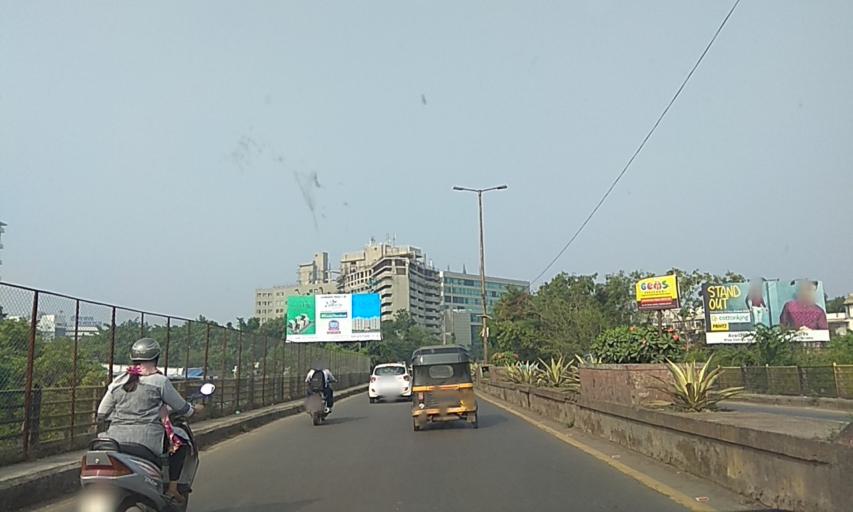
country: IN
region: Maharashtra
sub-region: Pune Division
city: Pune
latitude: 18.5046
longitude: 73.8368
